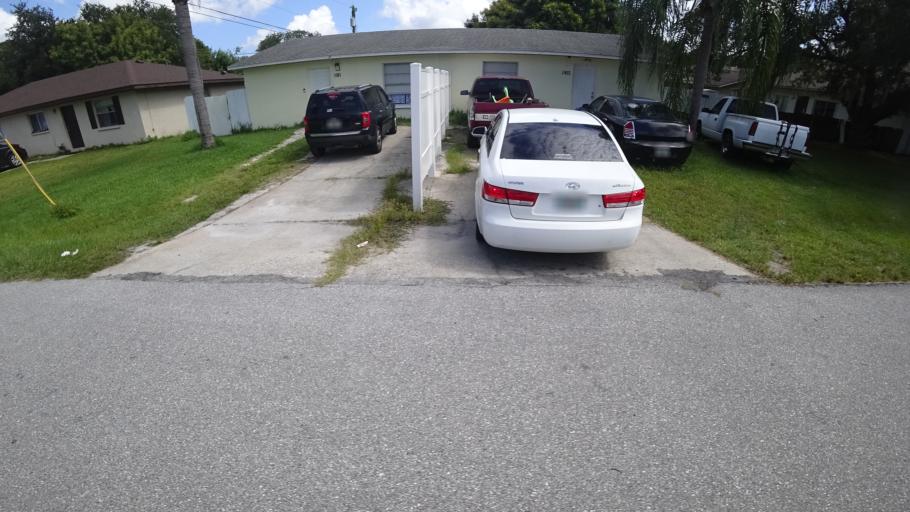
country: US
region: Florida
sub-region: Manatee County
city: Samoset
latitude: 27.4541
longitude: -82.5405
